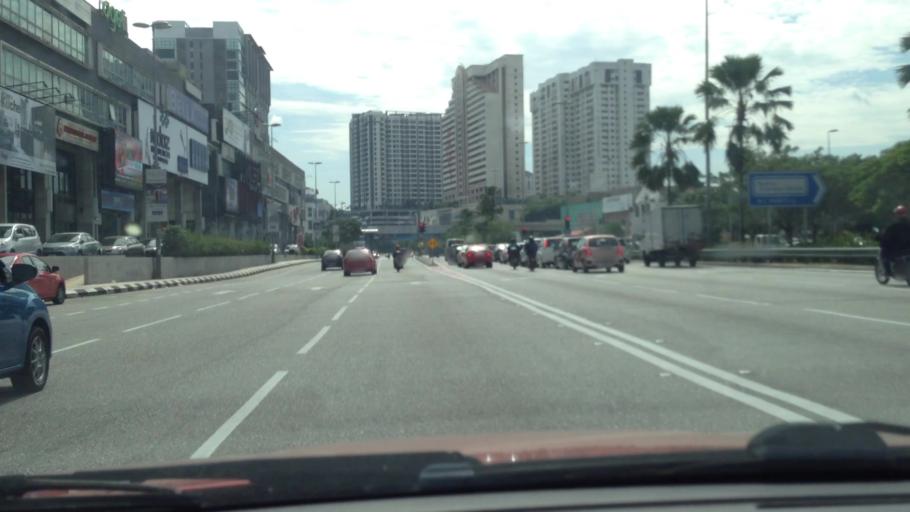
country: MY
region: Kuala Lumpur
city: Kuala Lumpur
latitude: 3.0827
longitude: 101.6691
